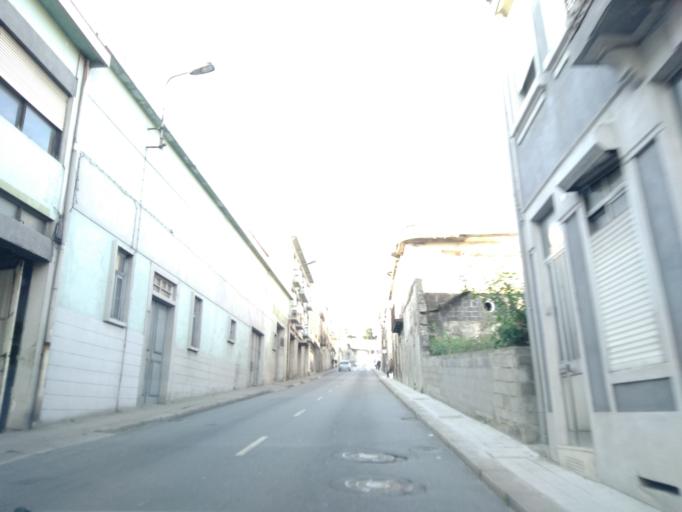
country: PT
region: Porto
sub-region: Vila Nova de Gaia
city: Oliveira do Douro
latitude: 41.1454
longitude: -8.5833
